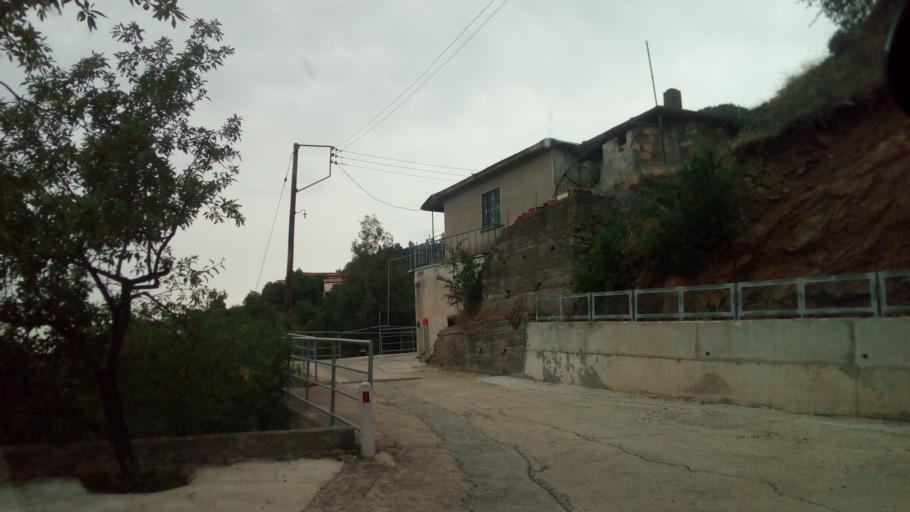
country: CY
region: Lefkosia
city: Kakopetria
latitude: 34.9635
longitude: 32.7525
